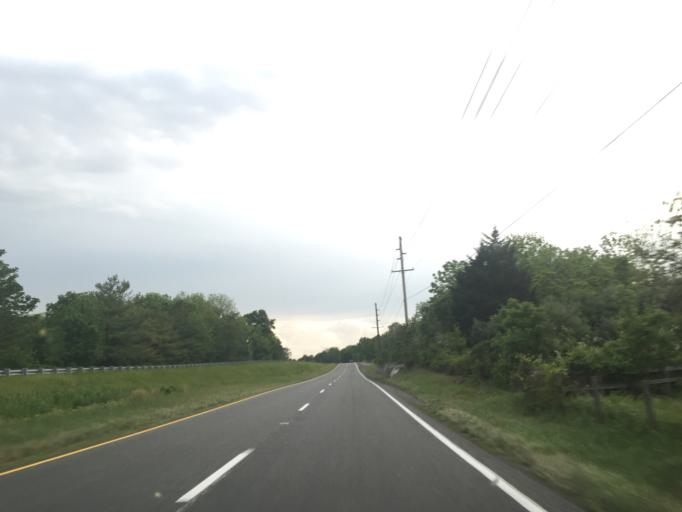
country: US
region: Virginia
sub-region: Clarke County
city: Berryville
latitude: 39.1850
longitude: -77.9457
